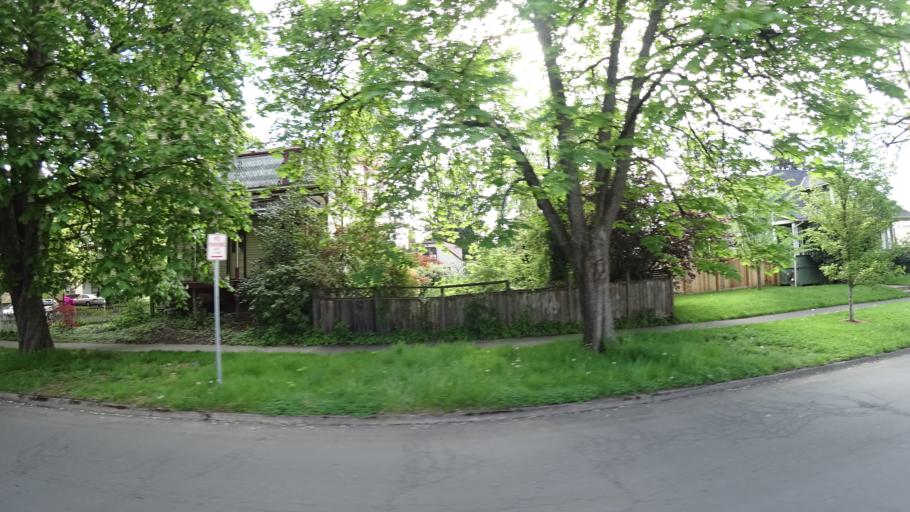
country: US
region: Oregon
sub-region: Washington County
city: Hillsboro
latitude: 45.5174
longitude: -122.9863
